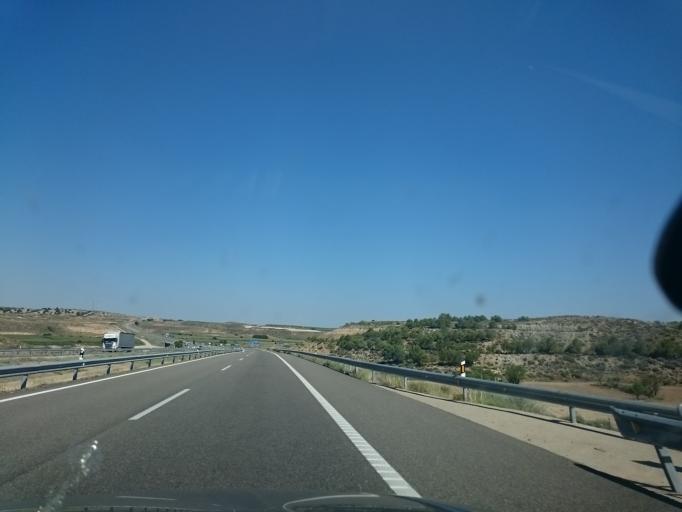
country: ES
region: Aragon
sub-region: Provincia de Huesca
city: Penalba
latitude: 41.5136
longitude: -0.0470
